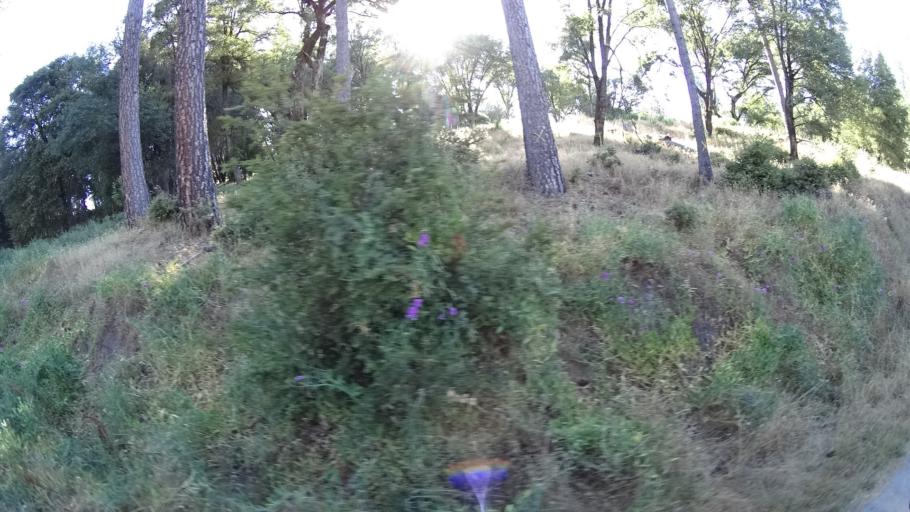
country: US
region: California
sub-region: Amador County
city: Pioneer
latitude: 38.3758
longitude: -120.5544
